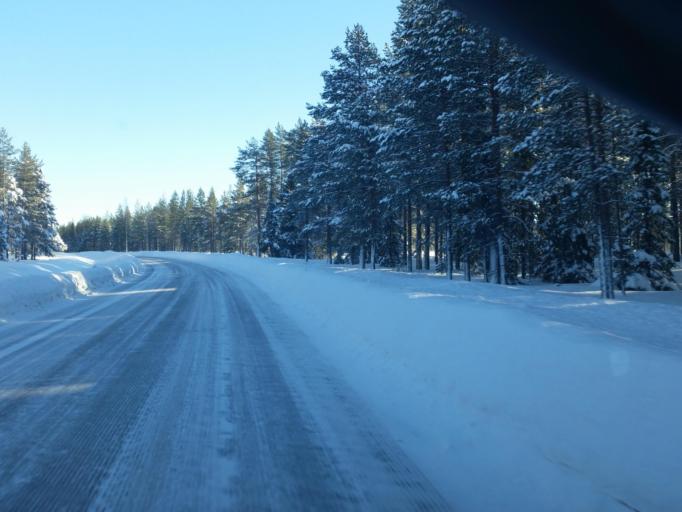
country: SE
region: Vaesterbotten
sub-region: Skelleftea Kommun
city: Storvik
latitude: 65.3355
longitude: 20.8840
